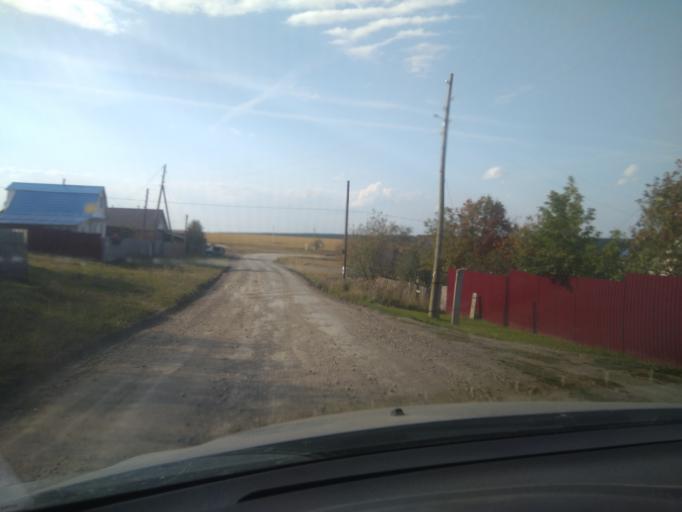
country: RU
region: Sverdlovsk
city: Pokrovskoye
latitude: 56.4351
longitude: 61.5894
